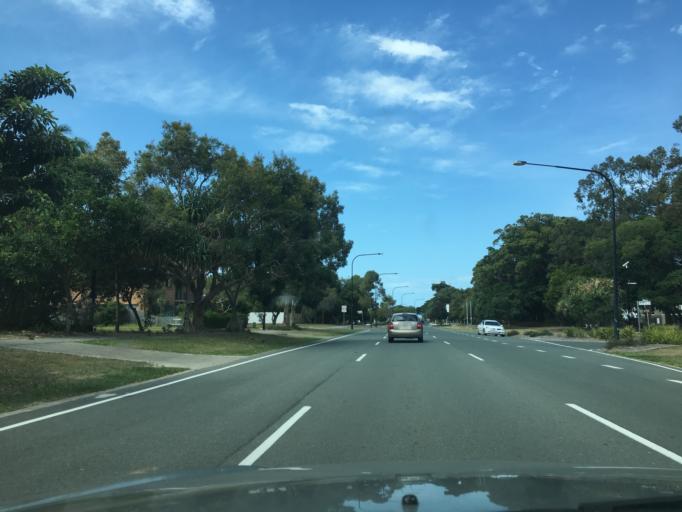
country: AU
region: Queensland
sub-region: Moreton Bay
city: Woorim
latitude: -27.0706
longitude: 153.2011
